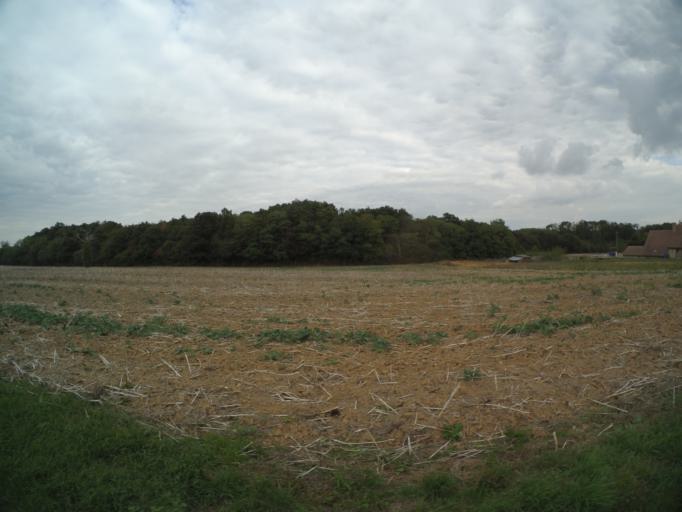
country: FR
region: Centre
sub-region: Departement d'Indre-et-Loire
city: Poce-sur-Cisse
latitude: 47.4958
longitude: 0.9764
